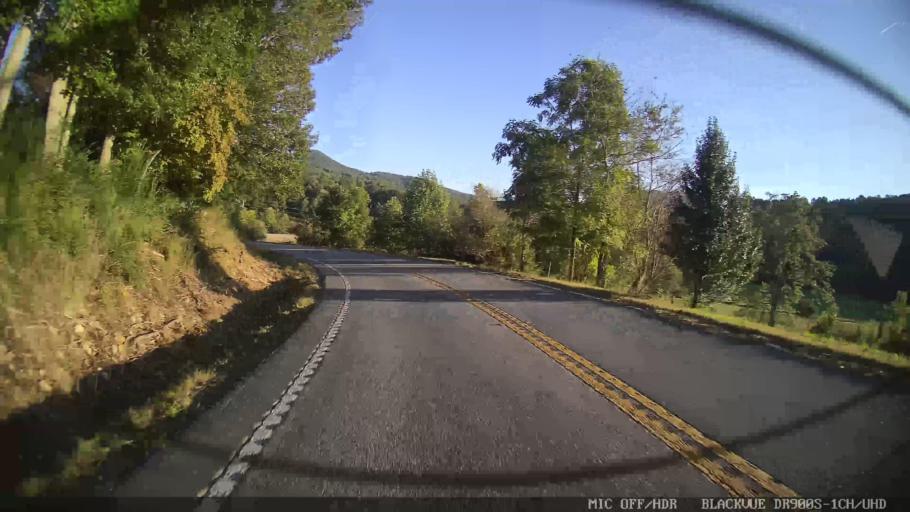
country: US
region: Georgia
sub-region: Fannin County
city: Blue Ridge
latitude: 34.8403
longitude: -84.1926
